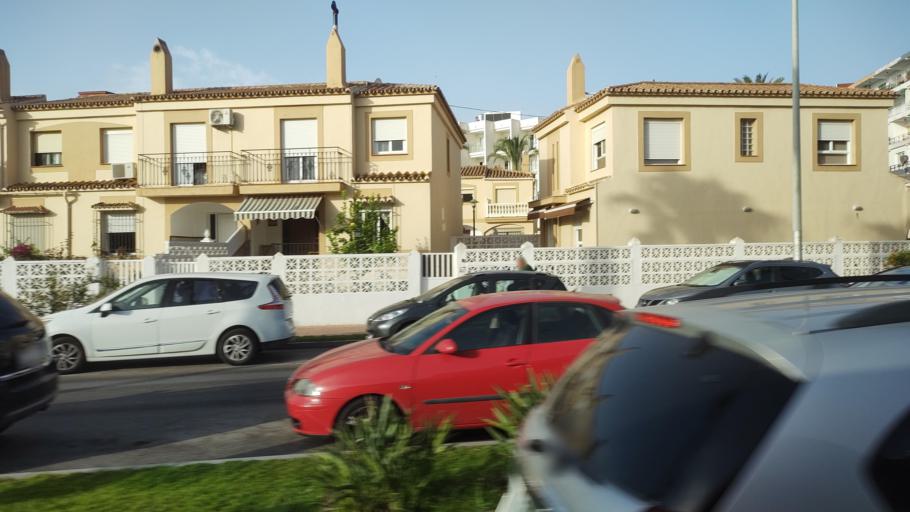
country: ES
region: Andalusia
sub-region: Provincia de Malaga
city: Torremolinos
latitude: 36.6425
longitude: -4.4810
